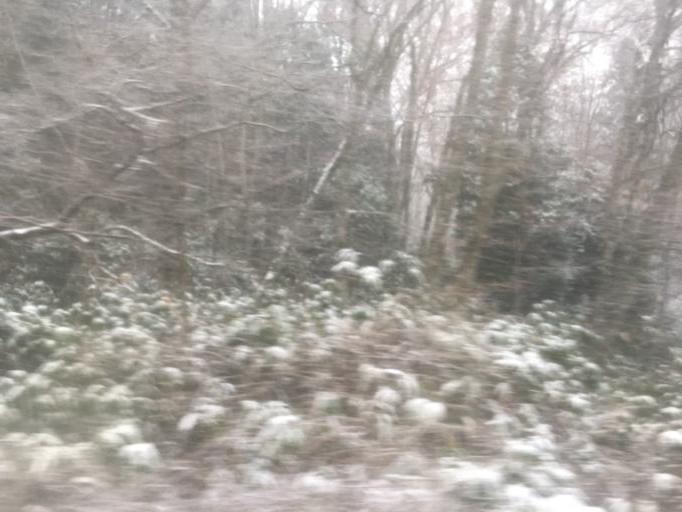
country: JP
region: Aomori
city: Goshogawara
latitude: 41.0989
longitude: 140.5283
